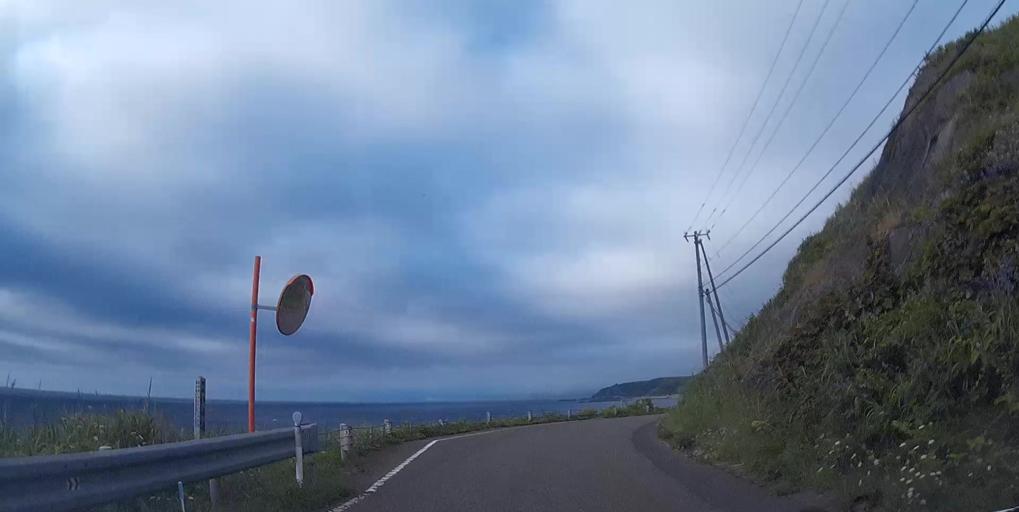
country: JP
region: Hokkaido
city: Iwanai
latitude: 42.3663
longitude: 139.8033
